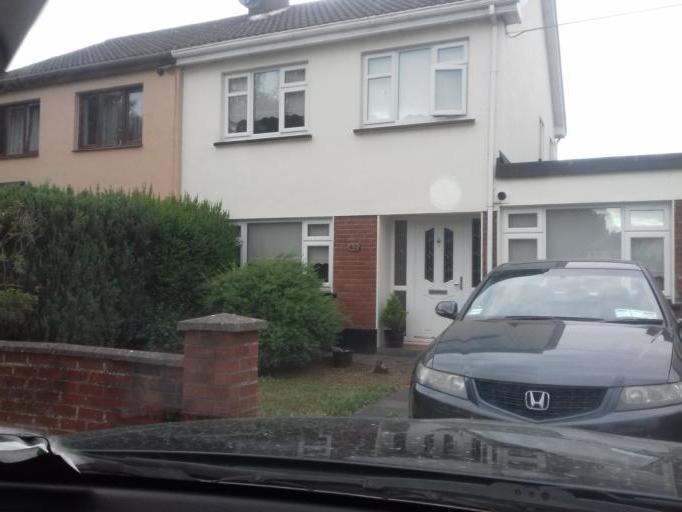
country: IE
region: Leinster
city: Hartstown
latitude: 53.3961
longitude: -6.4089
